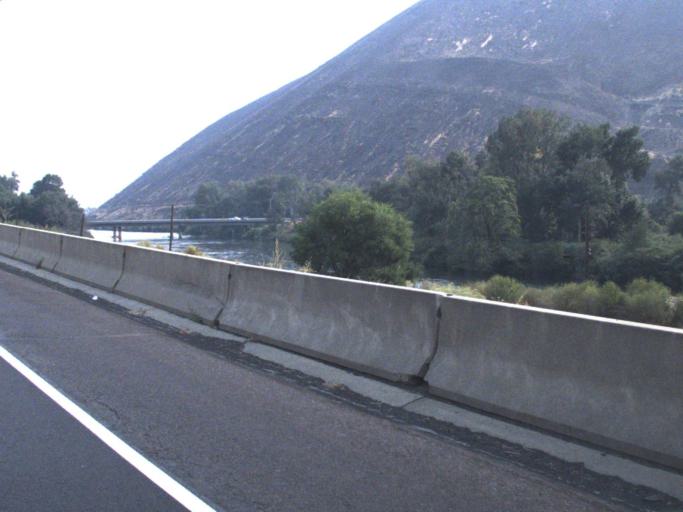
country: US
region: Washington
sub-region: Yakima County
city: Union Gap
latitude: 46.5270
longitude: -120.4766
